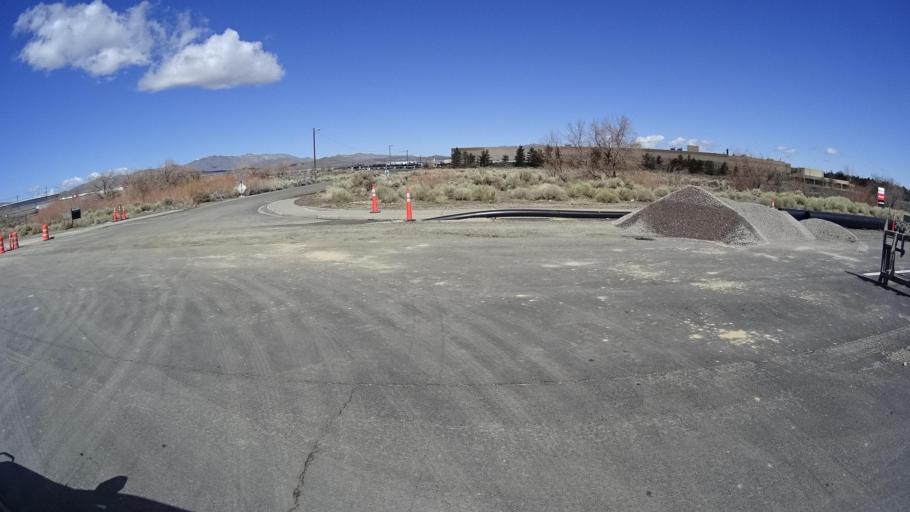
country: US
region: Nevada
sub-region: Washoe County
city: Lemmon Valley
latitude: 39.6425
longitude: -119.8869
